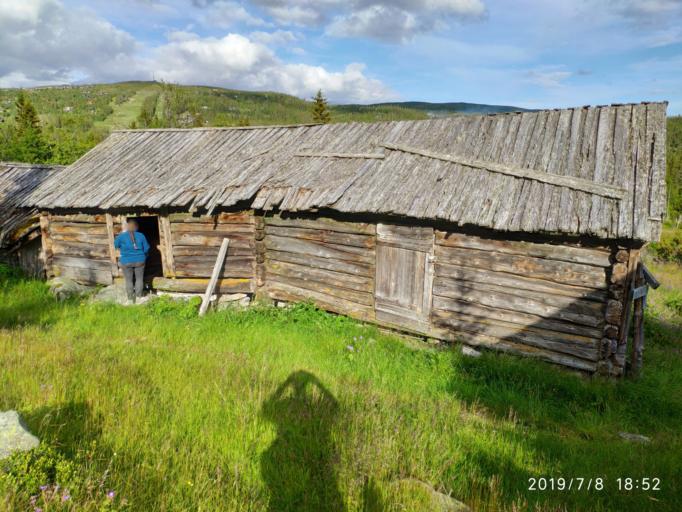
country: NO
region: Buskerud
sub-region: Nes
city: Nesbyen
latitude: 60.3438
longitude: 9.1794
